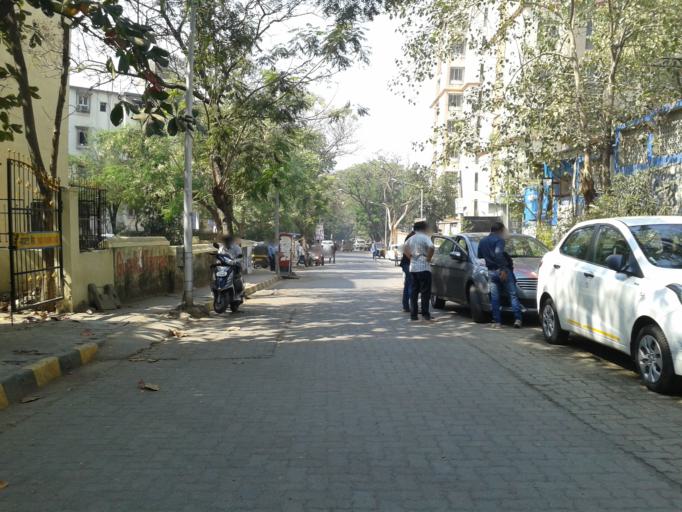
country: IN
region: Maharashtra
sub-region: Mumbai Suburban
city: Borivli
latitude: 19.2461
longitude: 72.8635
